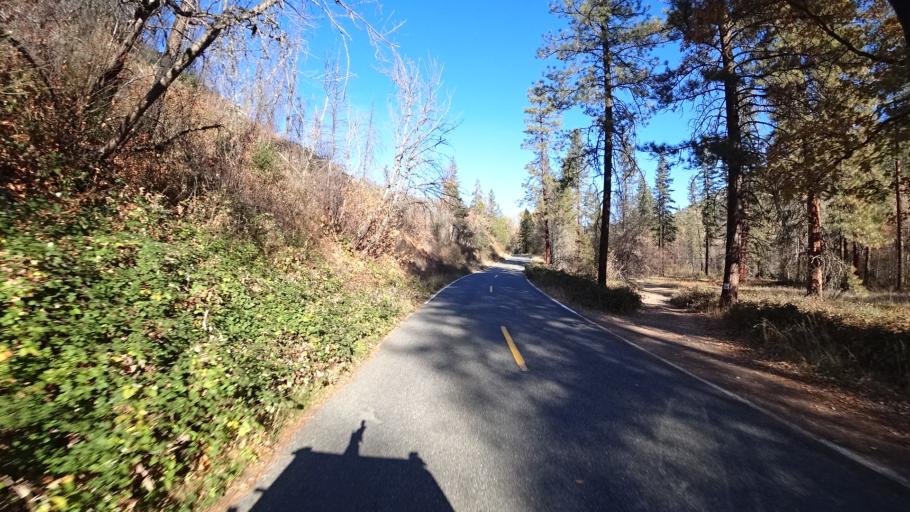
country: US
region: California
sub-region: Siskiyou County
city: Yreka
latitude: 41.8741
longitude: -122.8201
